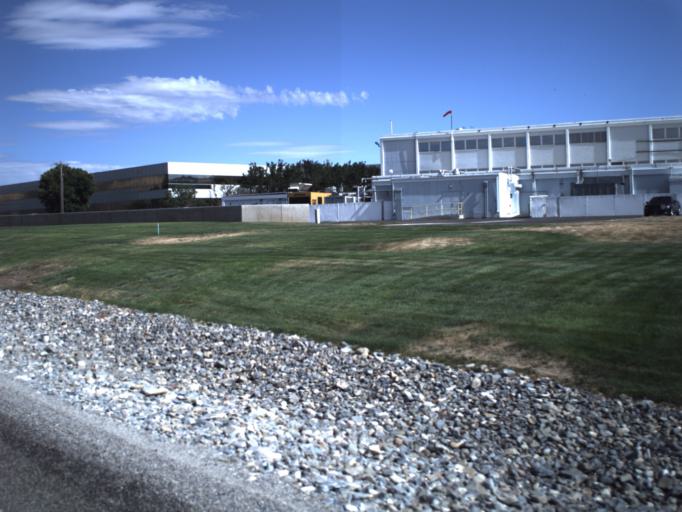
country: US
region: Utah
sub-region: Box Elder County
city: Tremonton
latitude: 41.6590
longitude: -112.4418
